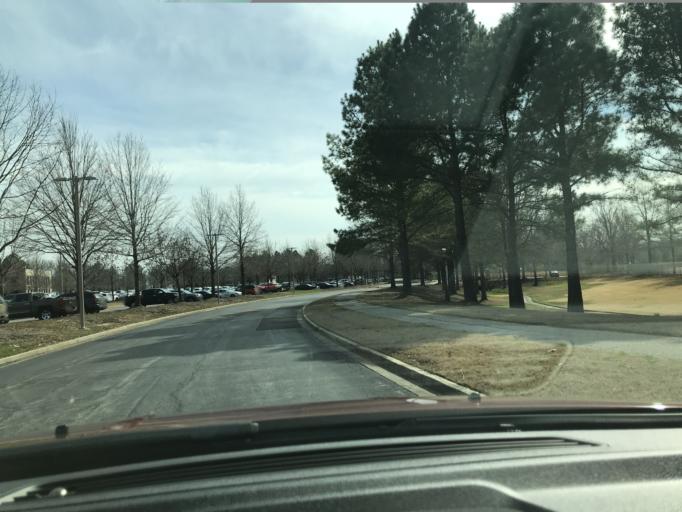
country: US
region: Tennessee
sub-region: Shelby County
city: Collierville
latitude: 35.0343
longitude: -89.7237
